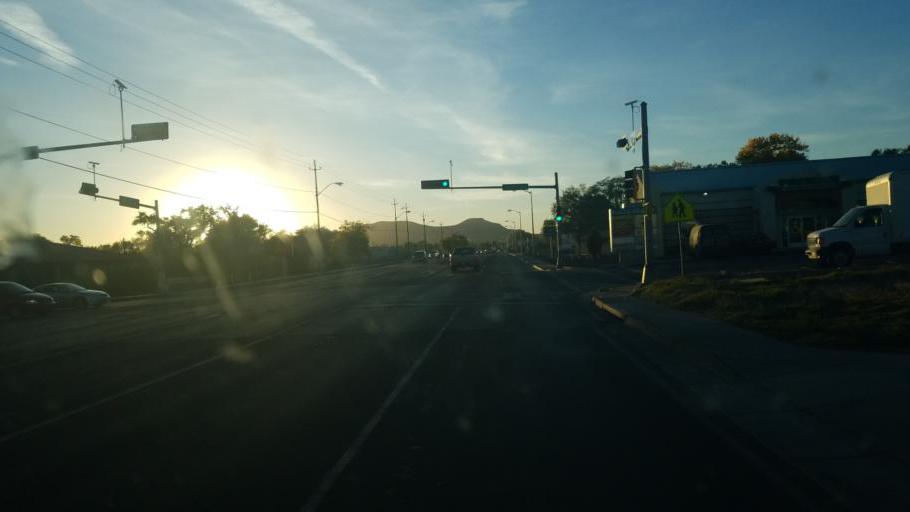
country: US
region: New Mexico
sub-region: Valencia County
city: Los Lunas
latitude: 34.8053
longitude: -106.7228
